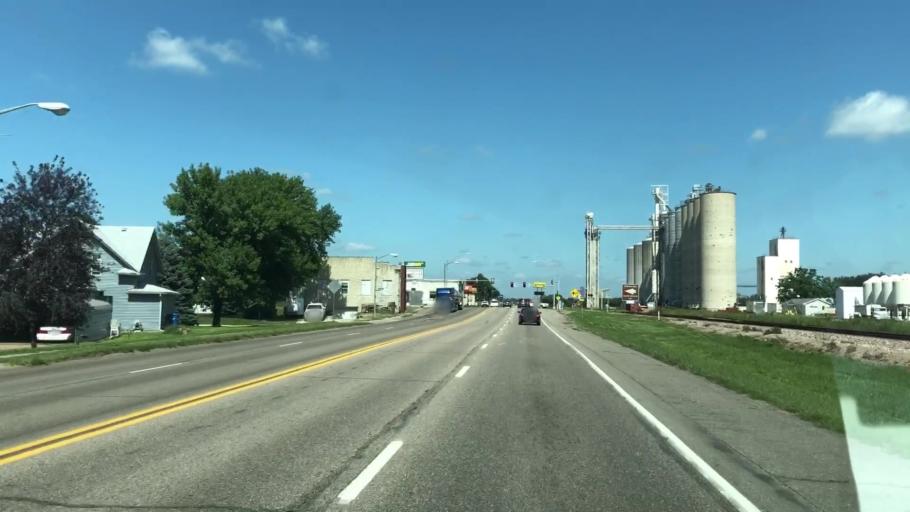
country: US
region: Iowa
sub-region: Woodbury County
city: Sioux City
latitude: 42.6249
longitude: -96.2924
